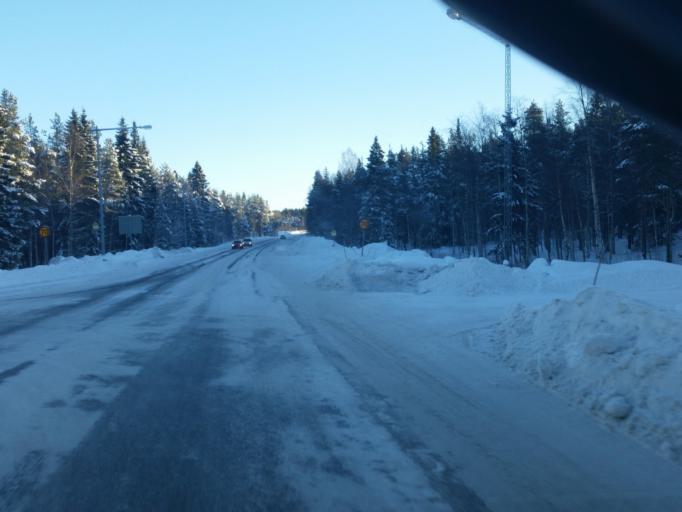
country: SE
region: Norrbotten
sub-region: Pitea Kommun
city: Bergsviken
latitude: 65.3306
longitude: 21.4272
